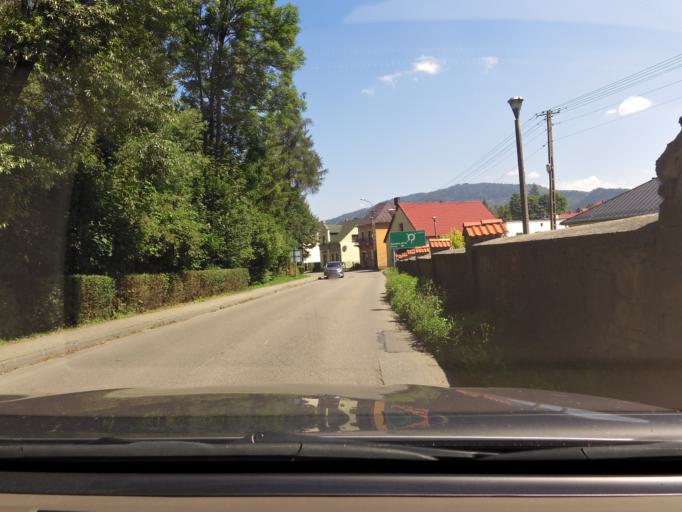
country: PL
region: Silesian Voivodeship
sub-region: Powiat zywiecki
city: Rajcza
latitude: 49.5013
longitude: 19.1009
